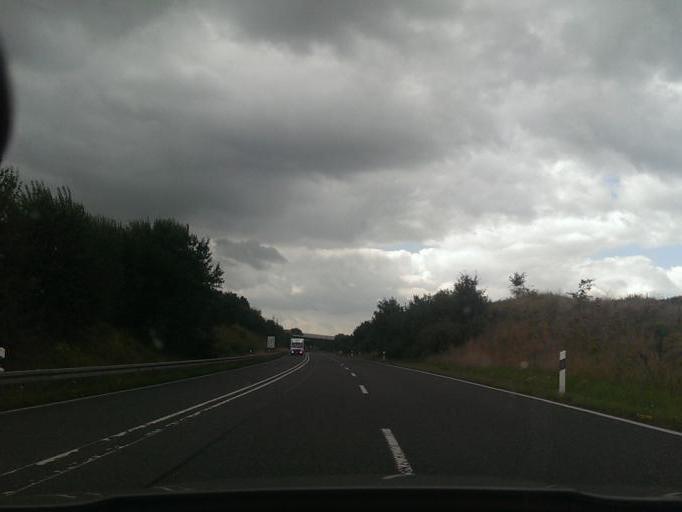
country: DE
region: Lower Saxony
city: Bevern
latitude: 51.8527
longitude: 9.5065
